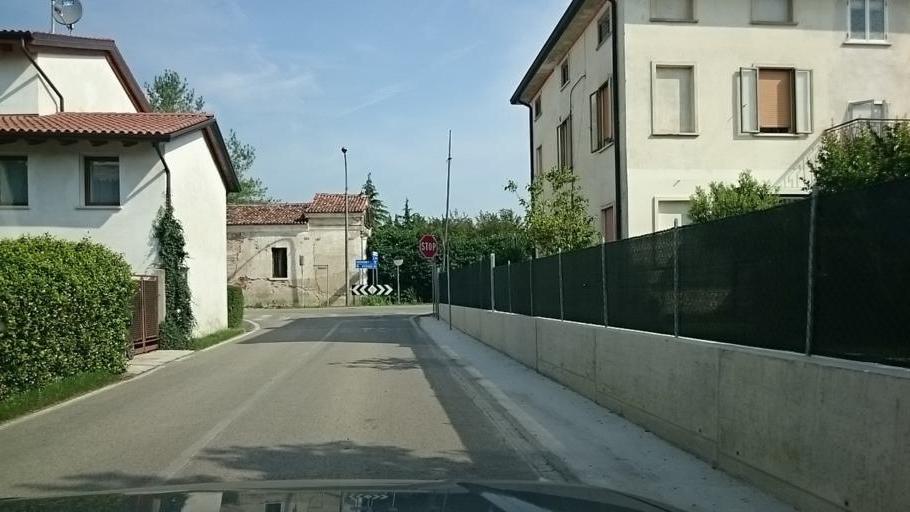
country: IT
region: Veneto
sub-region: Provincia di Treviso
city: Sant'Andrea
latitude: 45.6645
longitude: 11.9008
